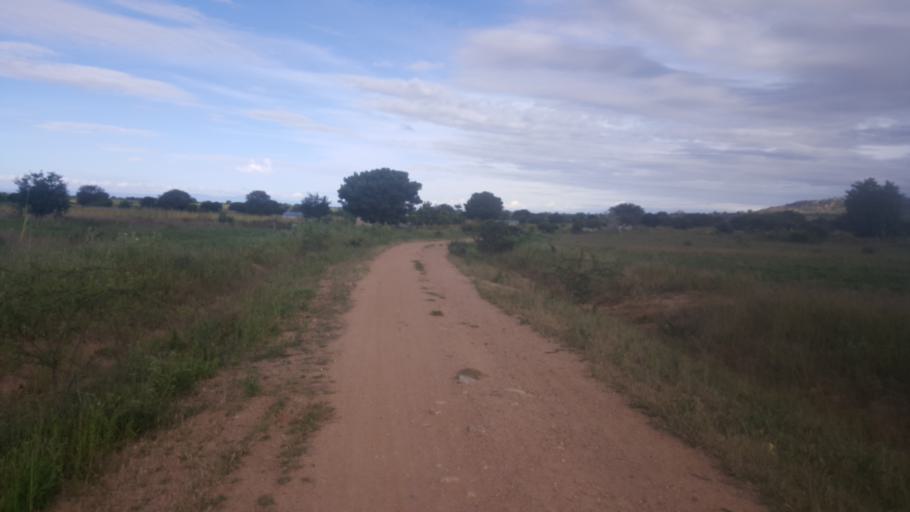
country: TZ
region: Dodoma
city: Dodoma
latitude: -6.0900
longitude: 35.5273
